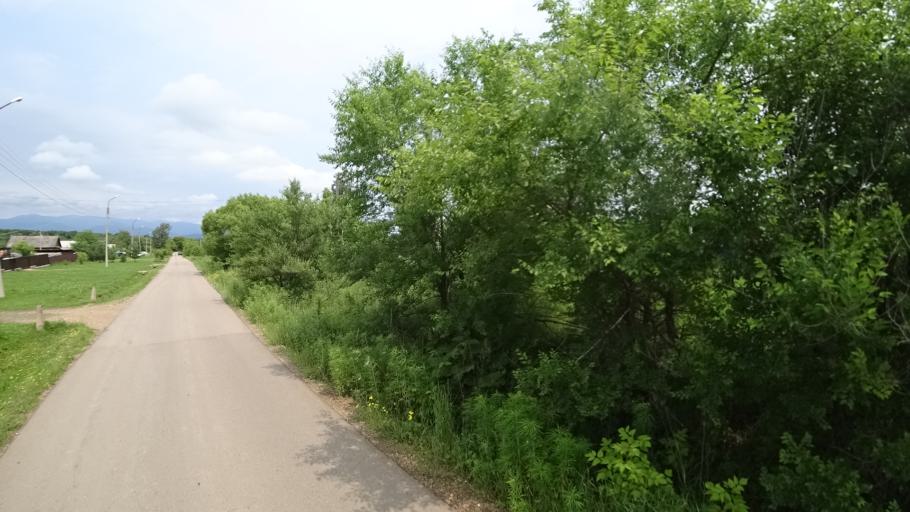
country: RU
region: Primorskiy
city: Novosysoyevka
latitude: 44.2361
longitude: 133.3588
